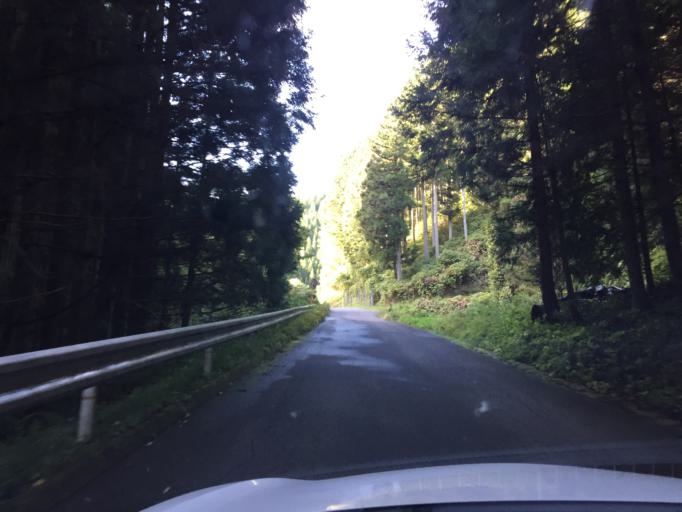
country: JP
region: Fukushima
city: Ishikawa
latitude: 37.1242
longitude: 140.5578
